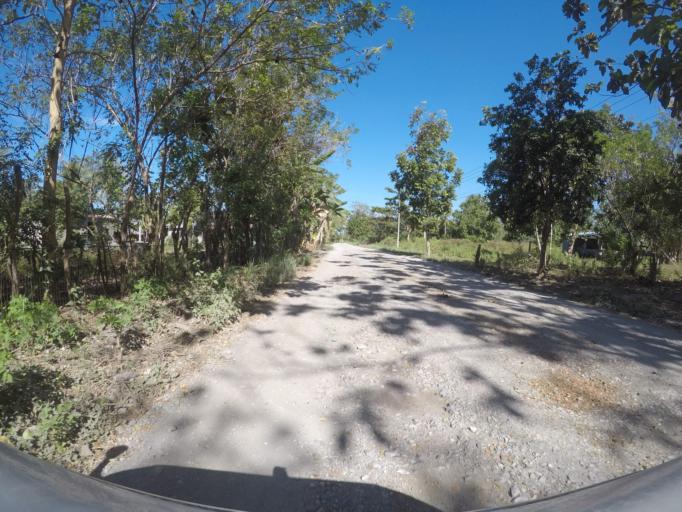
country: TL
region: Viqueque
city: Viqueque
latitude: -8.9337
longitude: 126.1331
